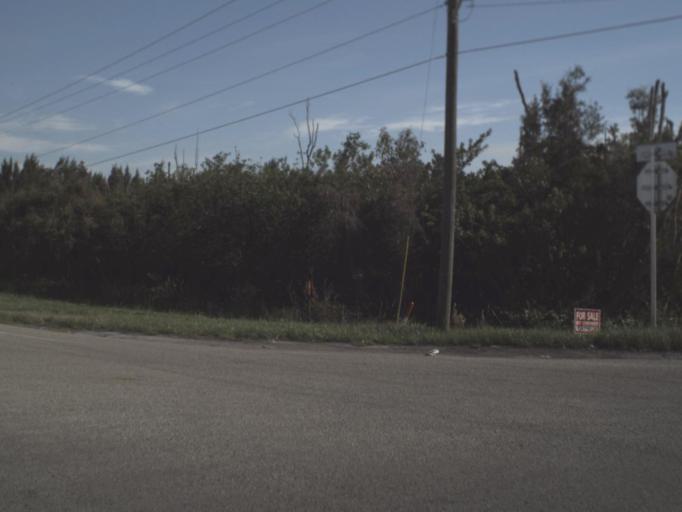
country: US
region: Florida
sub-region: Hendry County
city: Clewiston
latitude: 26.7505
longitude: -80.9019
